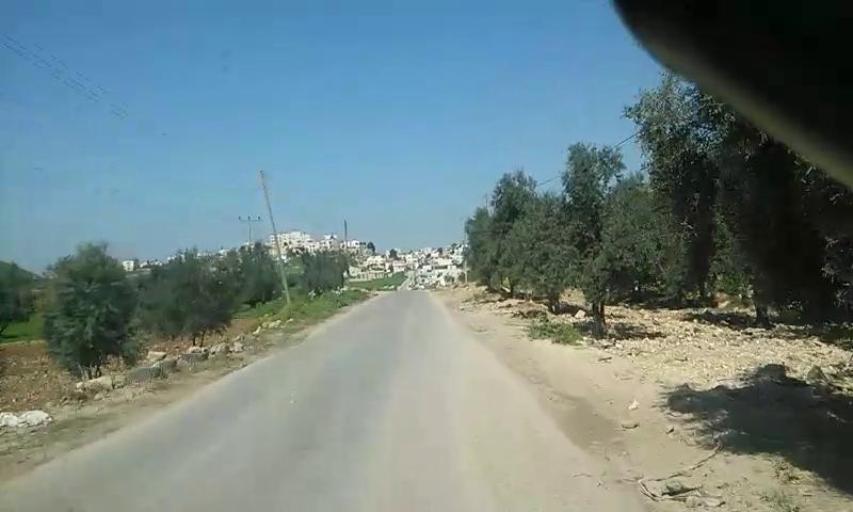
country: PS
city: Dayr Samit
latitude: 31.5125
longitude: 34.9704
